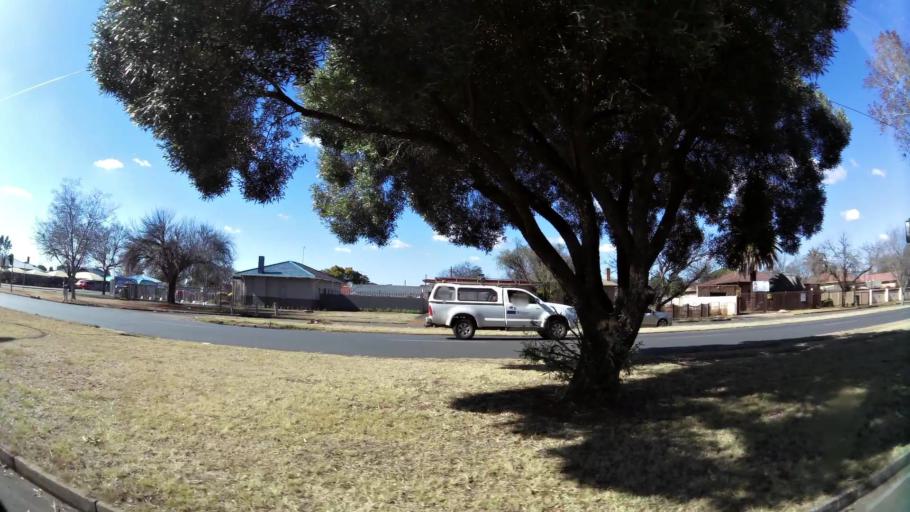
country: ZA
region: Gauteng
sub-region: West Rand District Municipality
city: Carletonville
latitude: -26.3601
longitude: 27.4012
